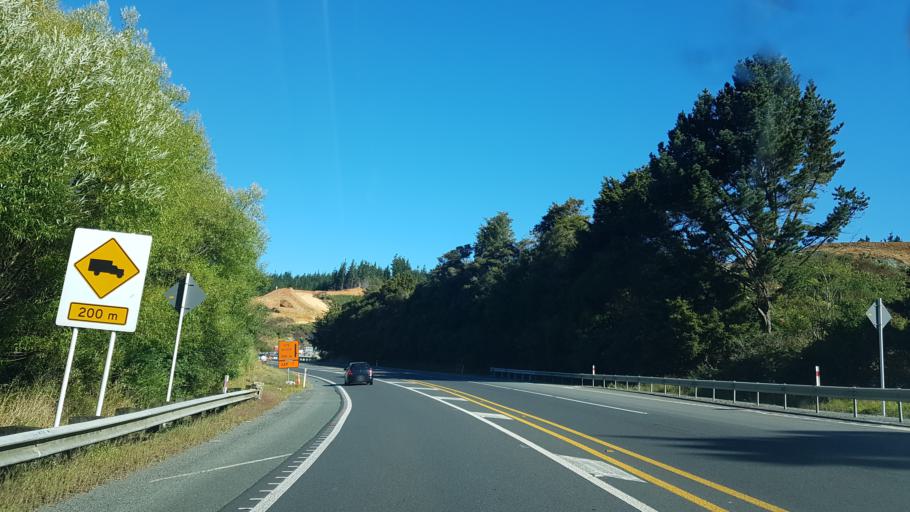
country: NZ
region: Auckland
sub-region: Auckland
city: Warkworth
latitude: -36.4926
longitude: 174.6587
